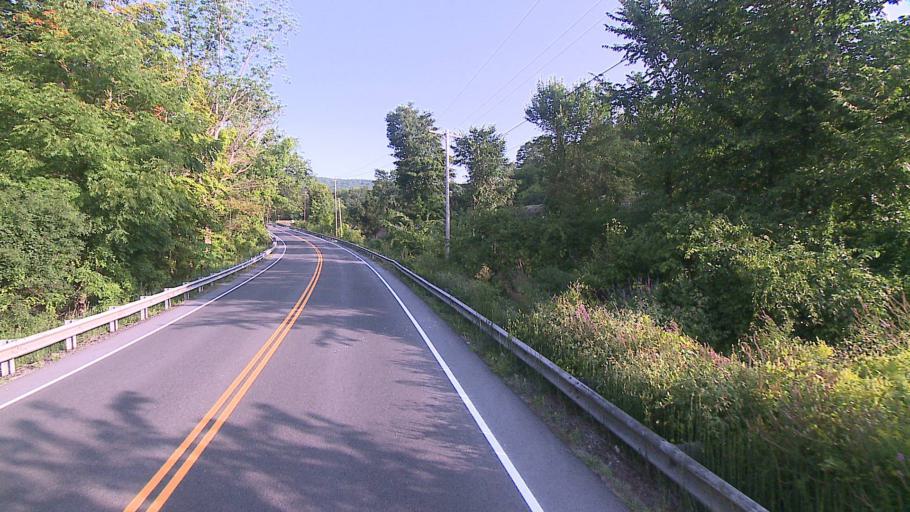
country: US
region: Connecticut
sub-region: Litchfield County
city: Kent
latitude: 41.6719
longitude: -73.5023
